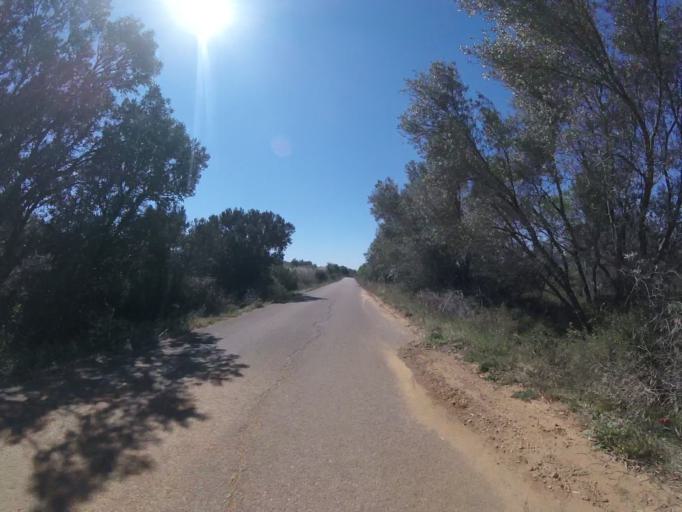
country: ES
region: Valencia
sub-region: Provincia de Castello
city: Cuevas de Vinroma
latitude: 40.3848
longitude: 0.1573
